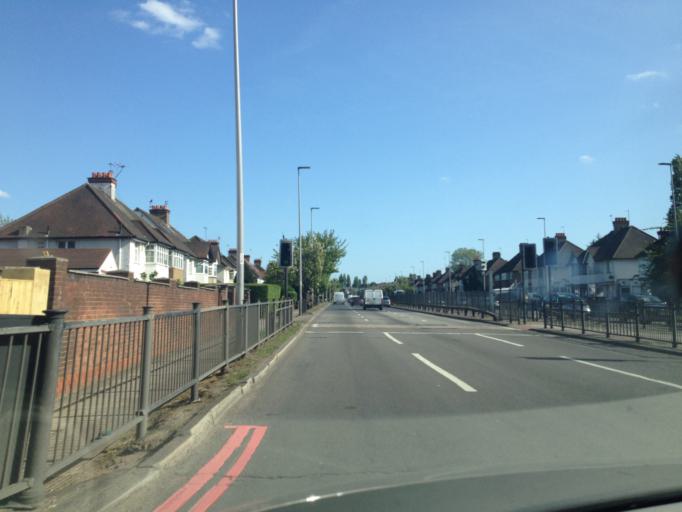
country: GB
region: England
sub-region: Greater London
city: Hendon
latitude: 51.5670
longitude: -0.2064
